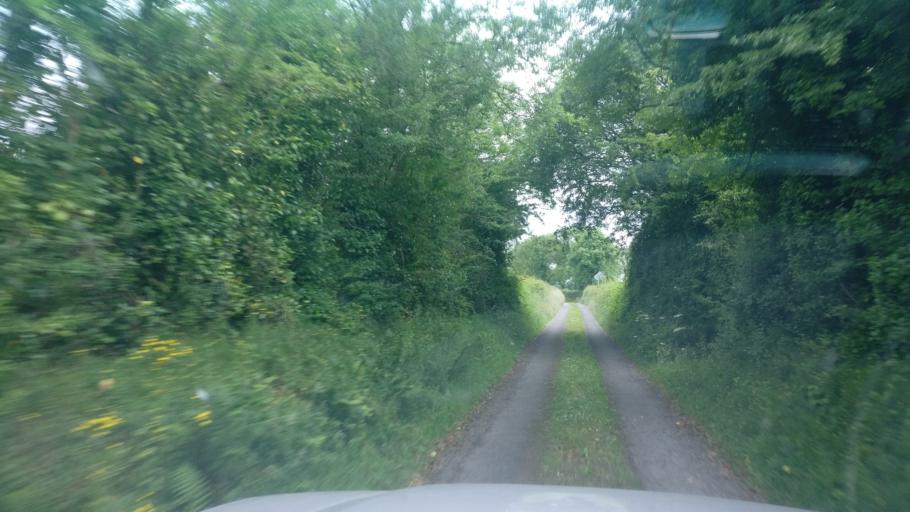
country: IE
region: Connaught
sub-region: County Galway
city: Ballinasloe
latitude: 53.2962
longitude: -8.3425
